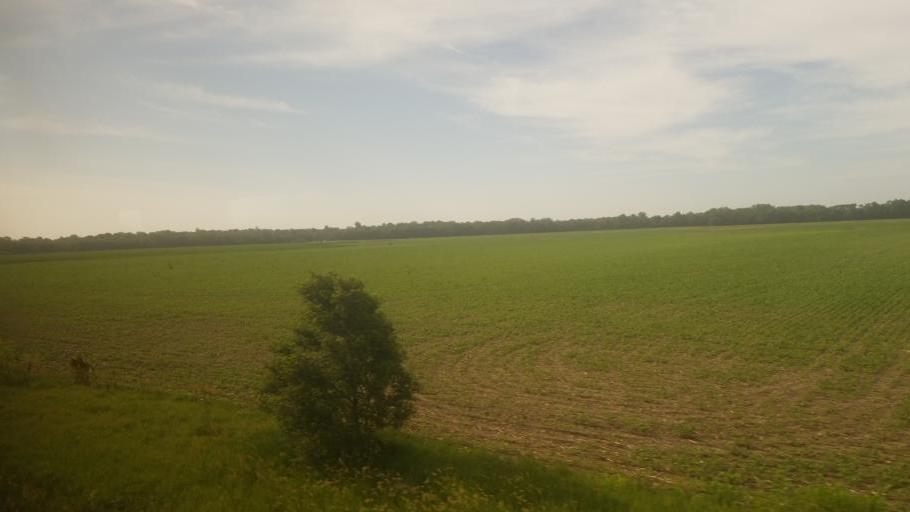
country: US
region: Kansas
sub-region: Douglas County
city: Eudora
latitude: 38.9496
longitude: -95.1249
